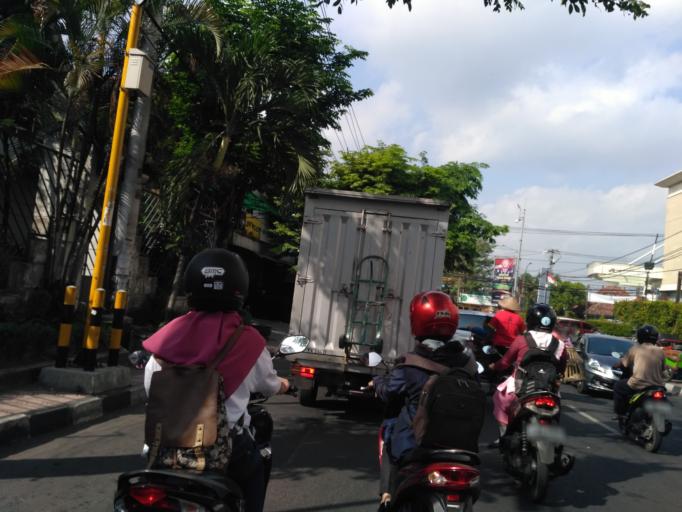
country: ID
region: Daerah Istimewa Yogyakarta
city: Yogyakarta
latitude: -7.8004
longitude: 110.3563
